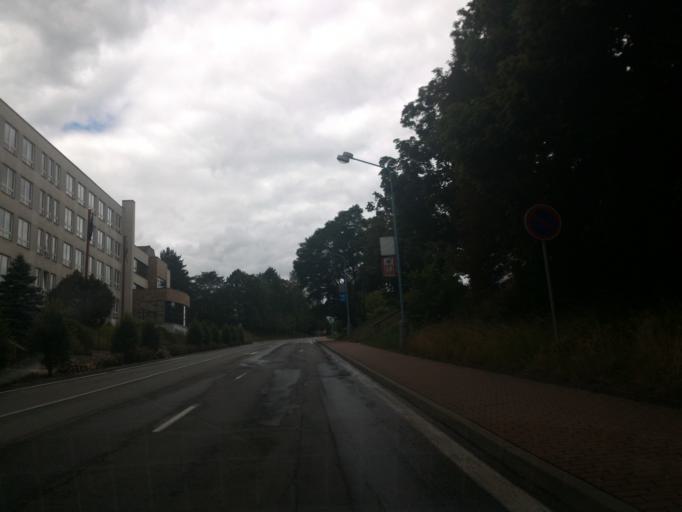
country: CZ
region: Vysocina
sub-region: Okres Pelhrimov
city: Pelhrimov
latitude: 49.4337
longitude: 15.2218
